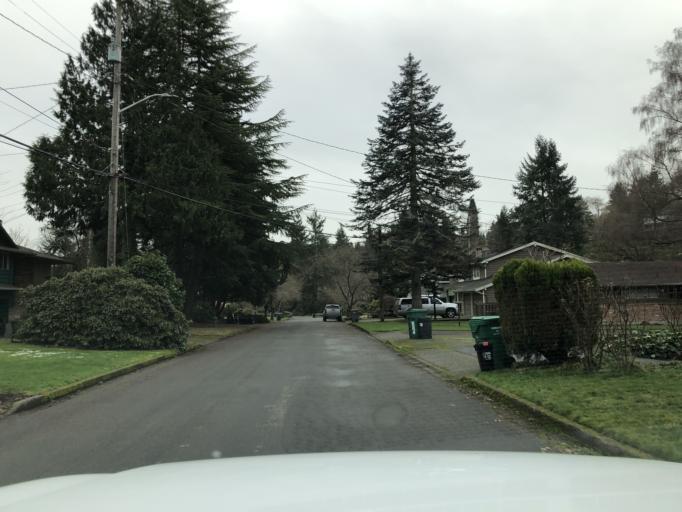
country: US
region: Washington
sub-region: King County
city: Inglewood-Finn Hill
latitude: 47.7017
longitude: -122.2814
